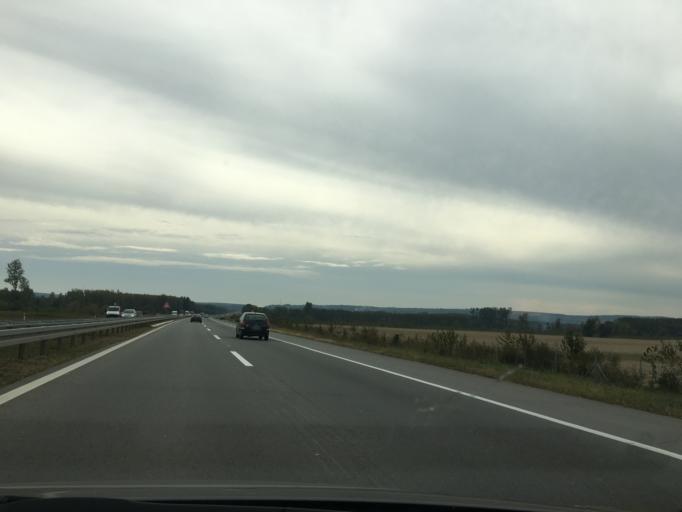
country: RS
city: Gardinovci
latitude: 45.1977
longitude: 20.0738
